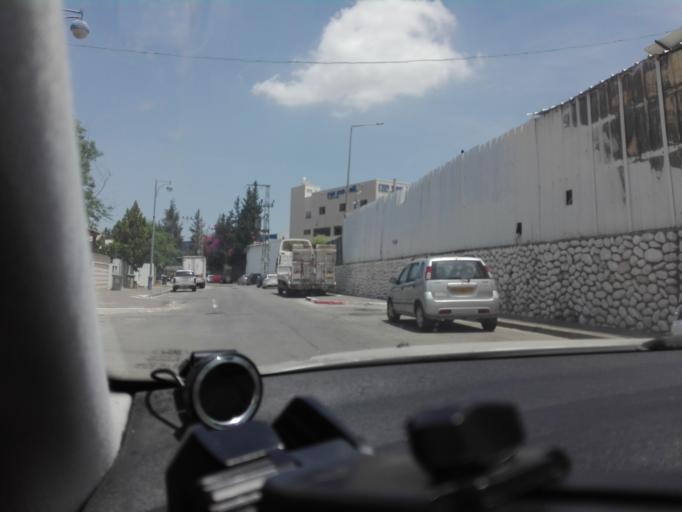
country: IL
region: Central District
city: Bene 'Ayish
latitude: 31.7339
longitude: 34.7529
